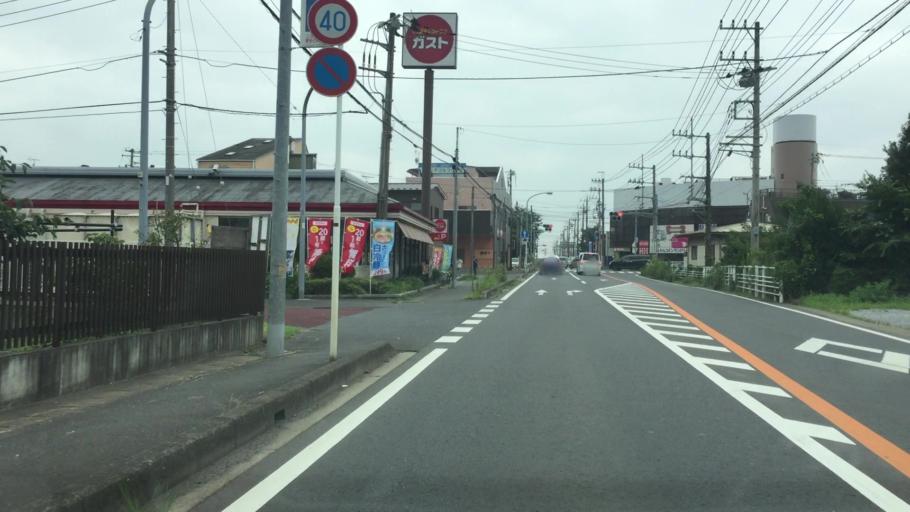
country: JP
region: Chiba
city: Abiko
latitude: 35.8329
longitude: 140.0043
